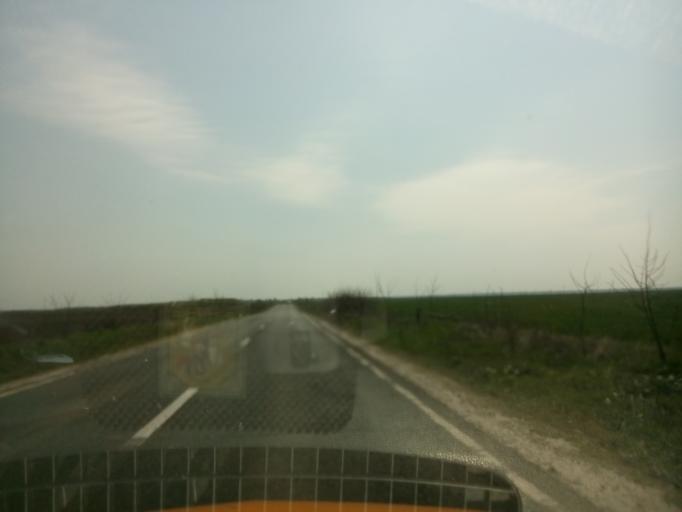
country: RO
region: Giurgiu
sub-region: Comuna Herasti
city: Herasti
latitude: 44.2427
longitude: 26.3876
